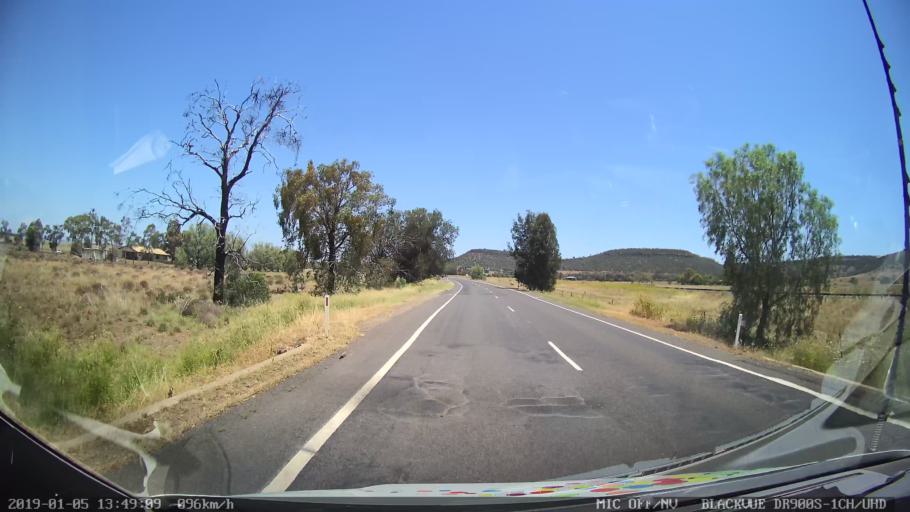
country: AU
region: New South Wales
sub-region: Gunnedah
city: Gunnedah
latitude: -31.0119
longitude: 150.2747
